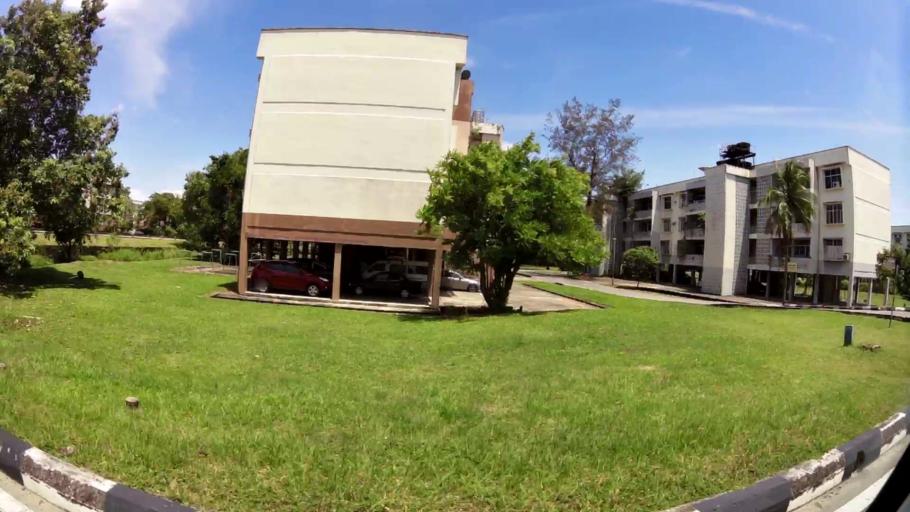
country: BN
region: Brunei and Muara
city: Bandar Seri Begawan
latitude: 4.9339
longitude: 114.9444
